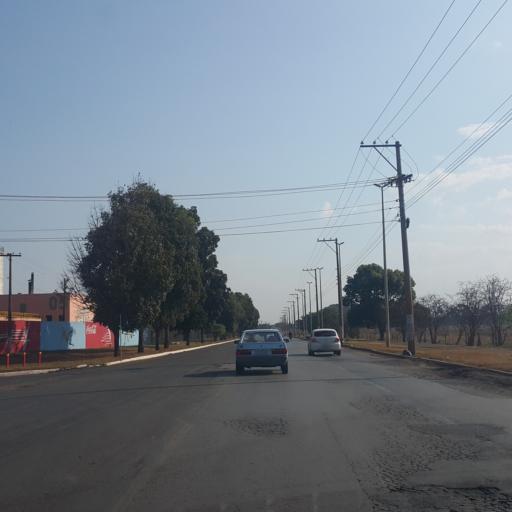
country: BR
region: Federal District
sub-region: Brasilia
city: Brasilia
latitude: -15.8696
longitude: -48.0391
